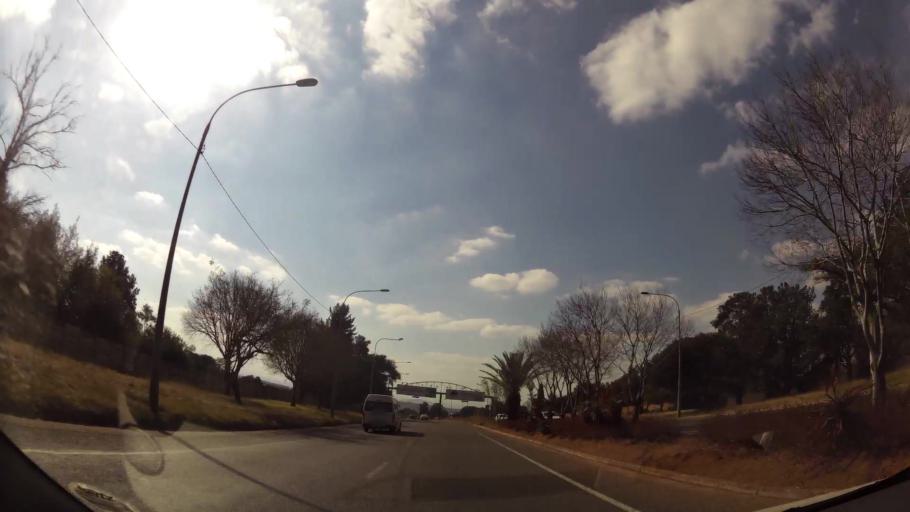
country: ZA
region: Gauteng
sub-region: West Rand District Municipality
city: Krugersdorp
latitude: -26.0833
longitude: 27.7891
